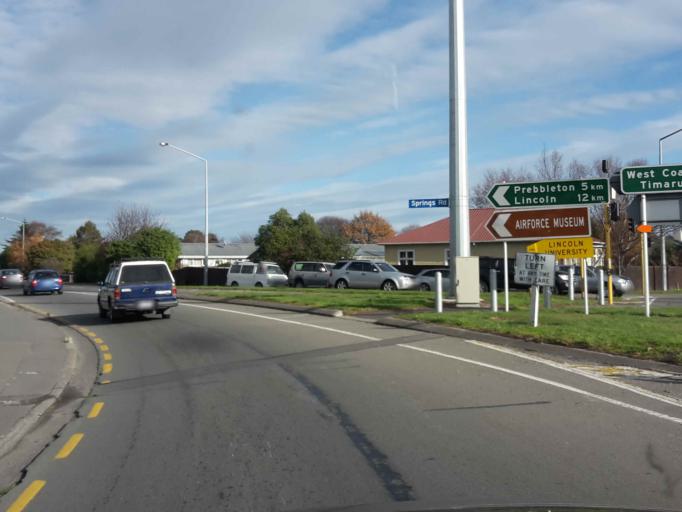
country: NZ
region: Canterbury
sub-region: Selwyn District
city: Prebbleton
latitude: -43.5434
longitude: 172.5463
